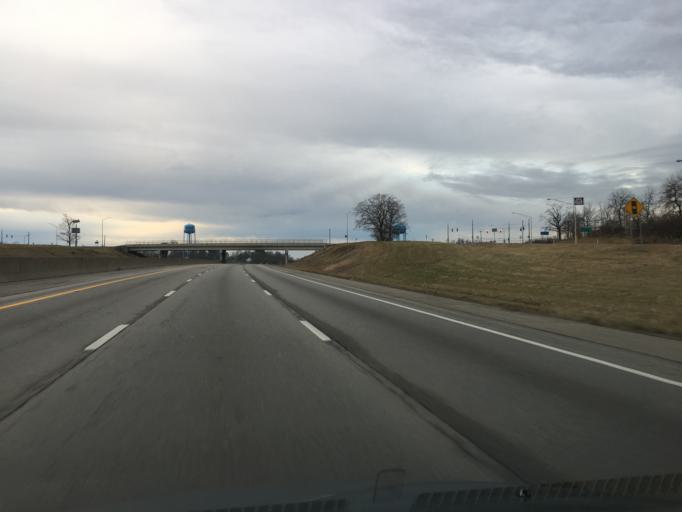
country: US
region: Kentucky
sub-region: Grant County
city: Crittenden
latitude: 38.7898
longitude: -84.6054
